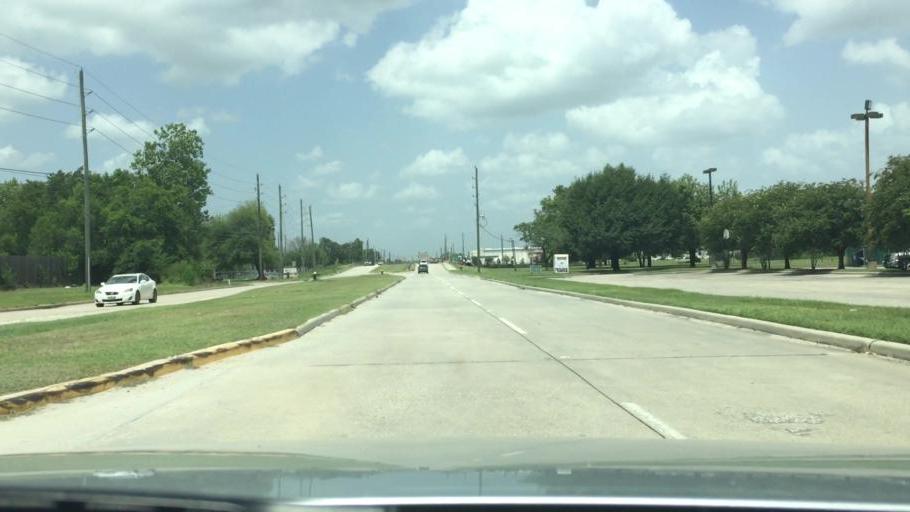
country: US
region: Texas
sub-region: Harris County
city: Hudson
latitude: 29.9470
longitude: -95.5181
